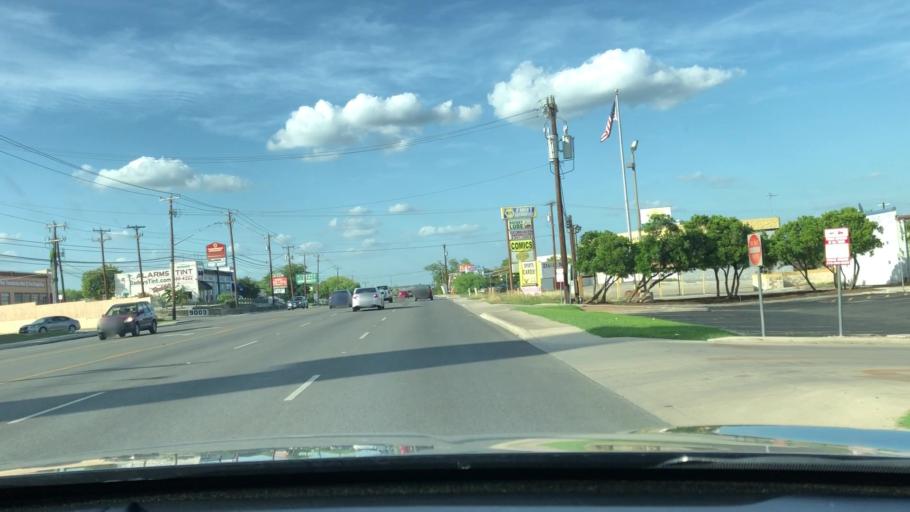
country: US
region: Texas
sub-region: Bexar County
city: Leon Valley
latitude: 29.5249
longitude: -98.5986
